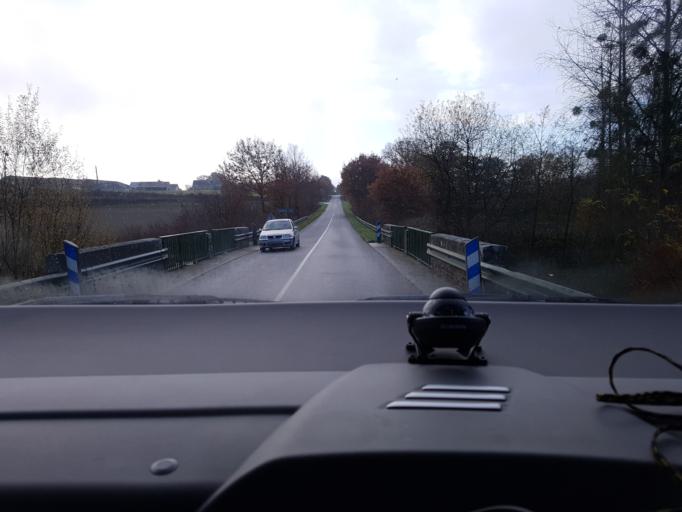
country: FR
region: Brittany
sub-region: Departement d'Ille-et-Vilaine
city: La Bouexiere
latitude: 48.1957
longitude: -1.4242
